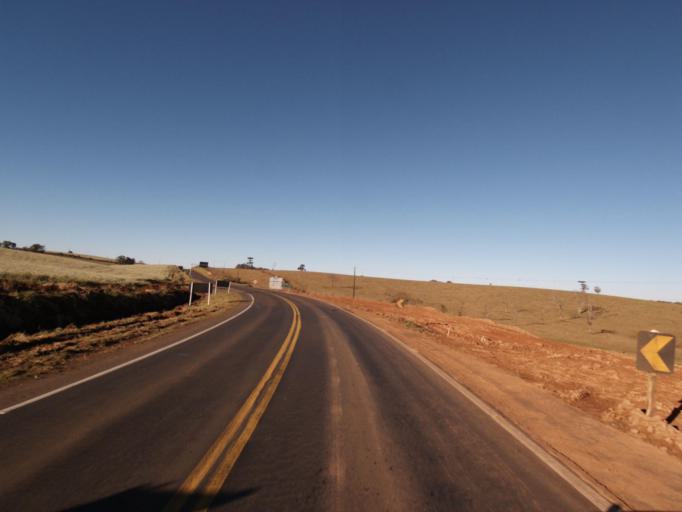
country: AR
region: Misiones
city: Bernardo de Irigoyen
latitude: -26.2886
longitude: -53.5560
